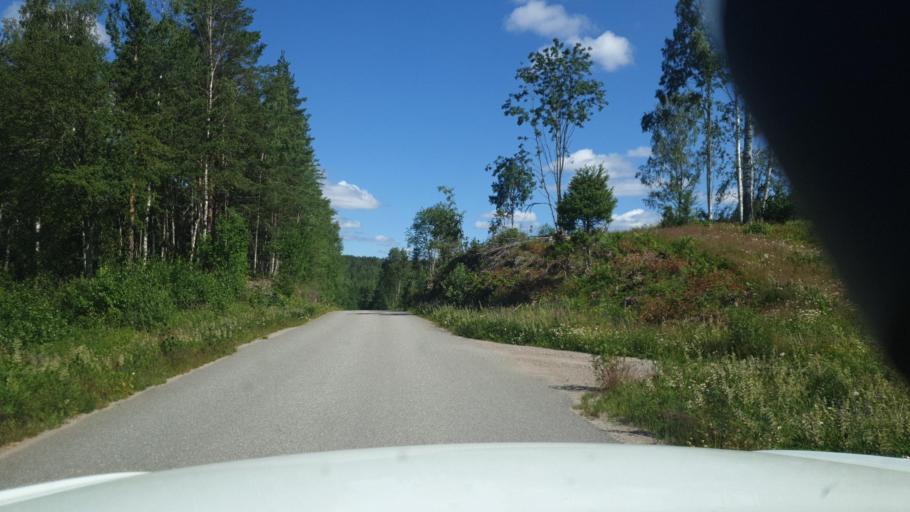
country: SE
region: Vaermland
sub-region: Eda Kommun
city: Amotfors
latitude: 59.8168
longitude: 12.3621
